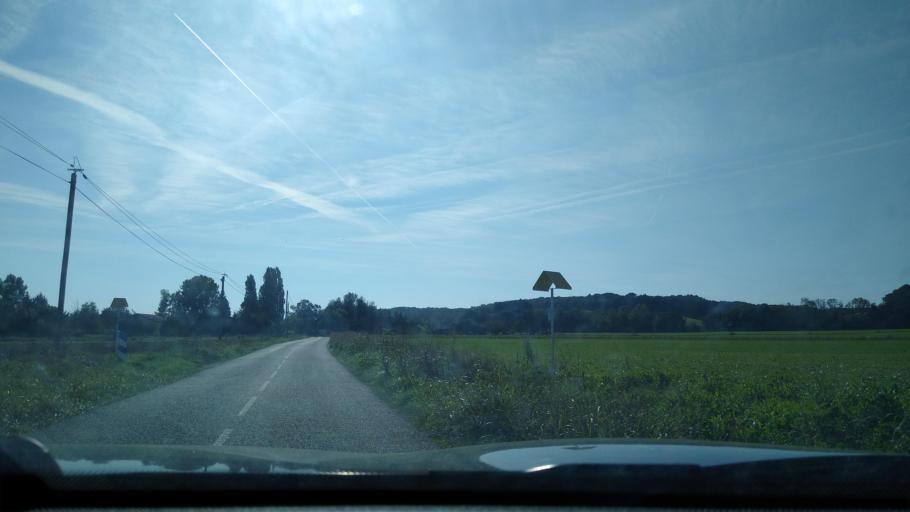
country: FR
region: Midi-Pyrenees
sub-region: Departement de la Haute-Garonne
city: Grenade
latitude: 43.7559
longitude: 1.2579
